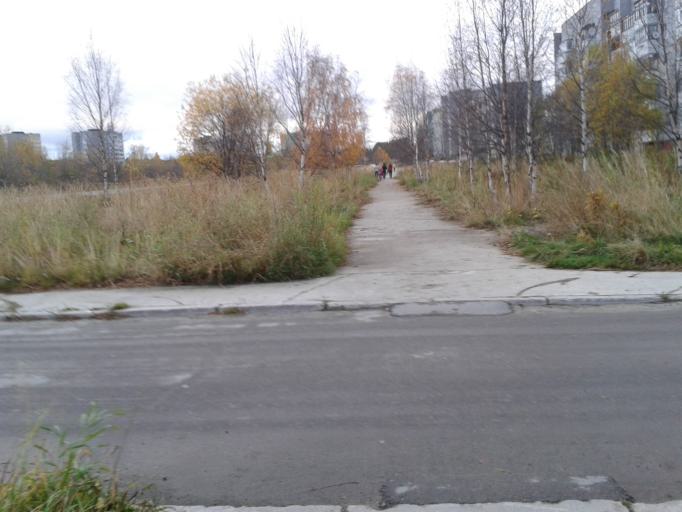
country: RU
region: Murmansk
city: Polyarnyye Zori
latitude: 67.3645
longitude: 32.4841
